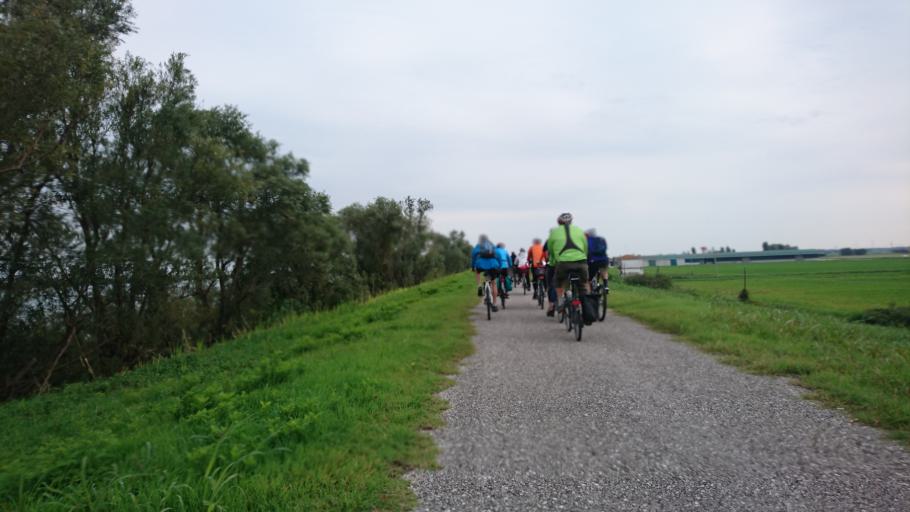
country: IT
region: Veneto
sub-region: Provincia di Rovigo
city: Ca' Tiepolo
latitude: 44.9570
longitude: 12.3827
